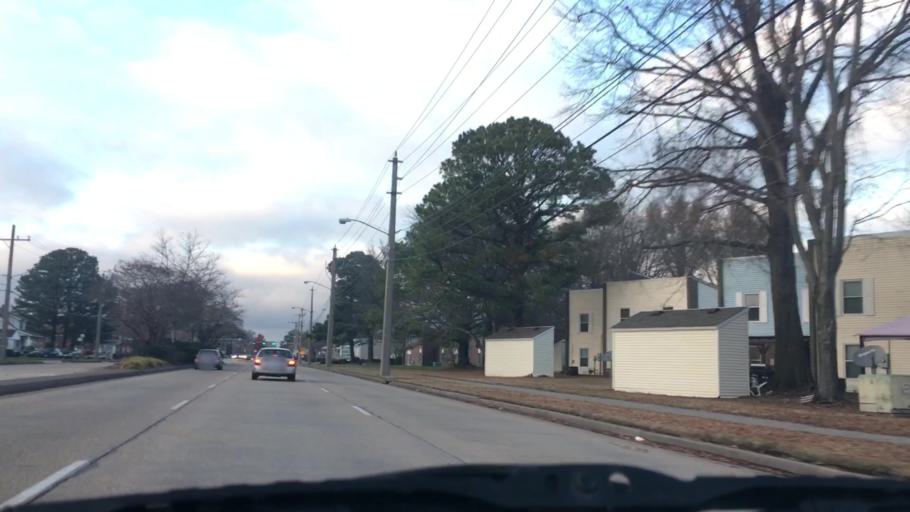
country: US
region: Virginia
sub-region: City of Norfolk
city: Norfolk
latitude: 36.9117
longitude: -76.2409
